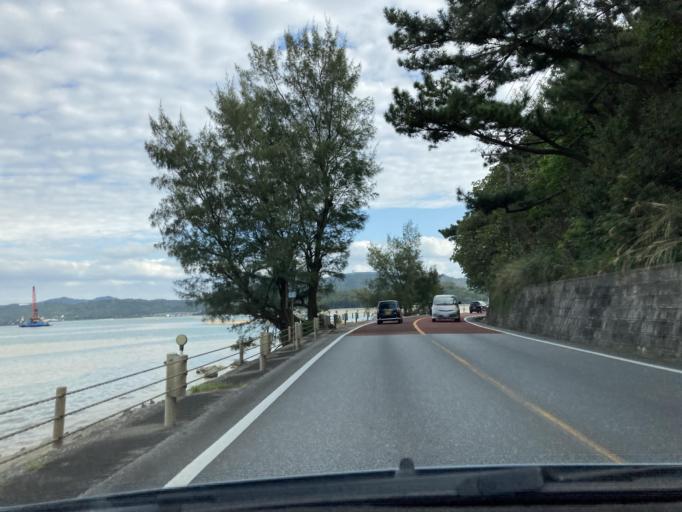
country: JP
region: Okinawa
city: Nago
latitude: 26.6382
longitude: 128.0032
